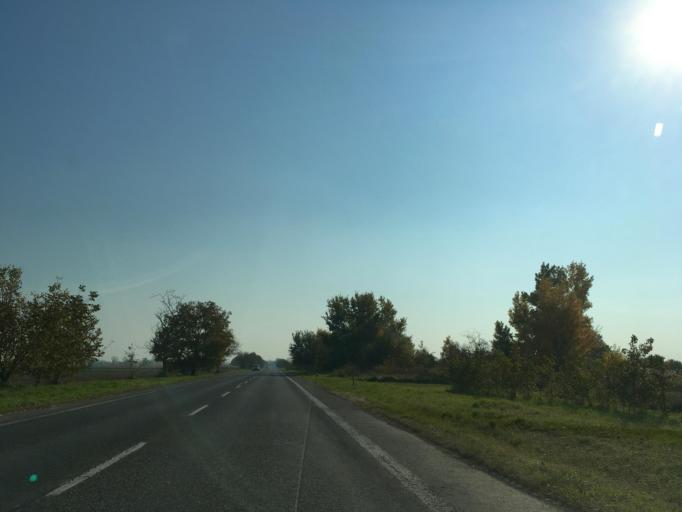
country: SK
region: Trnavsky
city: Samorin
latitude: 48.0520
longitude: 17.2894
